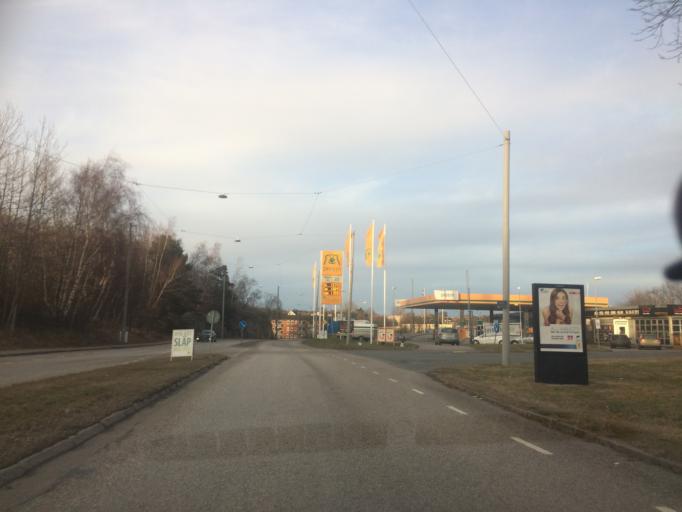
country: SE
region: Vaestra Goetaland
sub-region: Goteborg
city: Majorna
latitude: 57.6473
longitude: 11.8903
